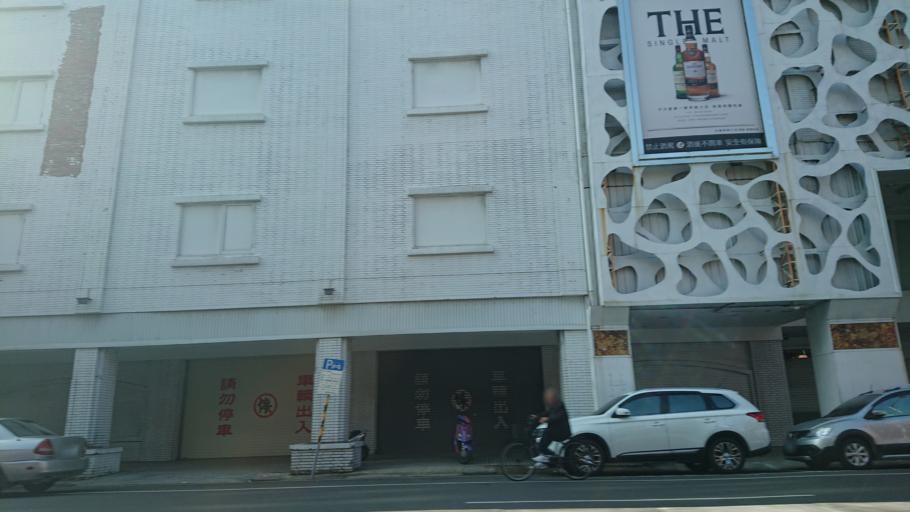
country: TW
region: Taiwan
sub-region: Tainan
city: Tainan
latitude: 22.9960
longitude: 120.1942
